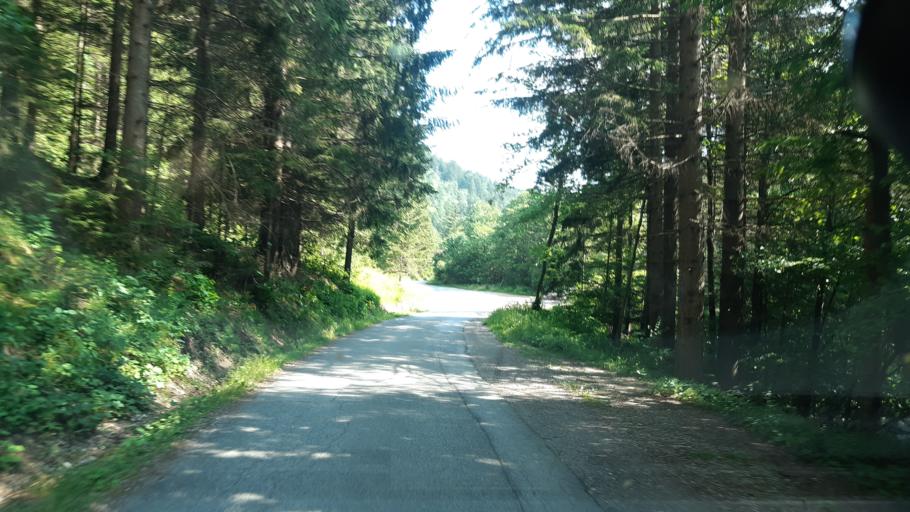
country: SI
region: Radovljica
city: Radovljica
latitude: 46.3852
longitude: 14.2177
